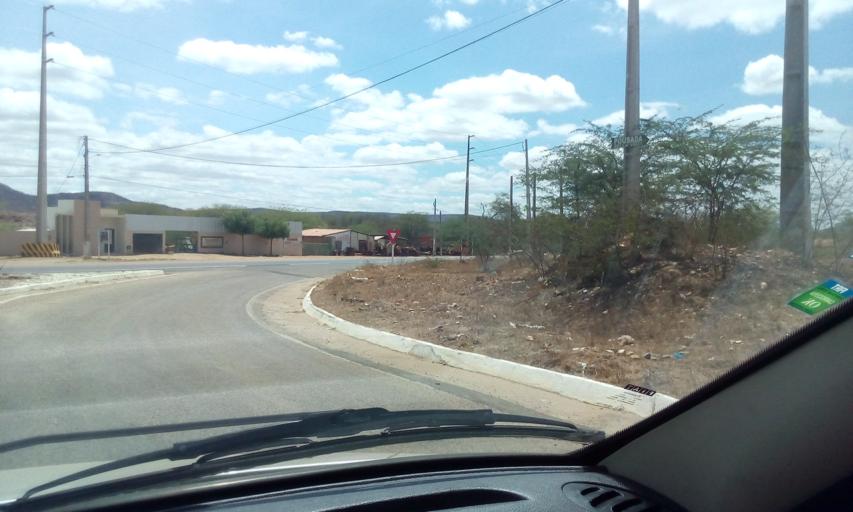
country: BR
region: Rio Grande do Norte
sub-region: Currais Novos
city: Currais Novos
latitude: -6.2776
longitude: -36.5228
